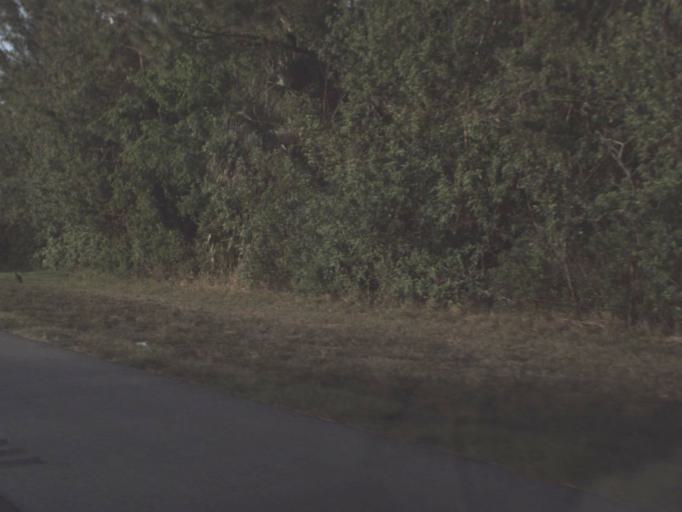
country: US
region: Florida
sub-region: Brevard County
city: Port Saint John
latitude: 28.5171
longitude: -80.8507
